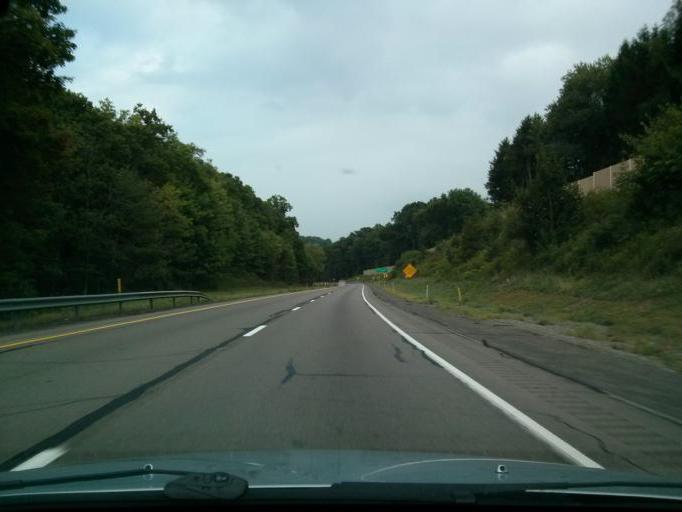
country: US
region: Pennsylvania
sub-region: Jefferson County
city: Brookville
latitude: 41.1694
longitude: -79.0811
